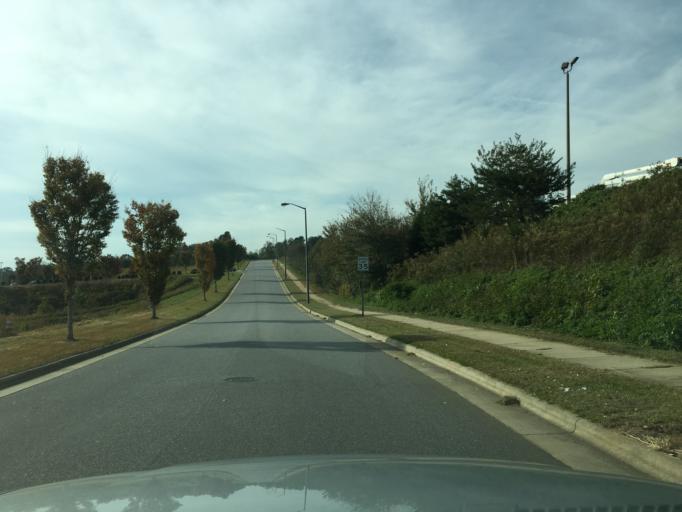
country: US
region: North Carolina
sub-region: Catawba County
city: Saint Stephens
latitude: 35.7263
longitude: -81.2836
